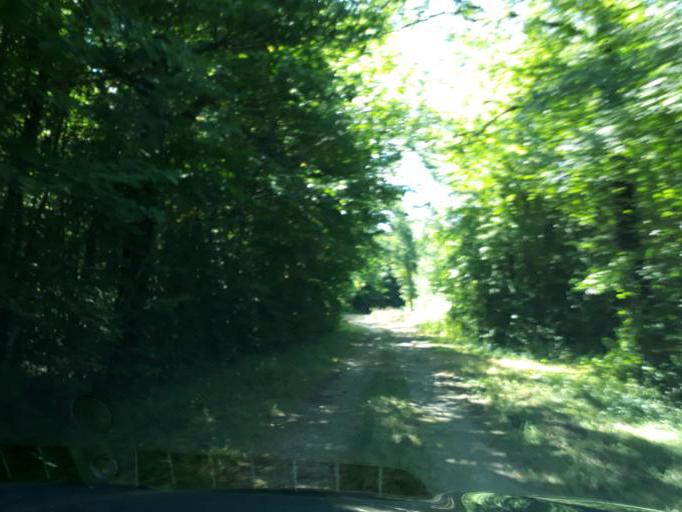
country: FR
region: Centre
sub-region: Departement du Loiret
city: Chevilly
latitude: 47.9932
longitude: 1.8953
